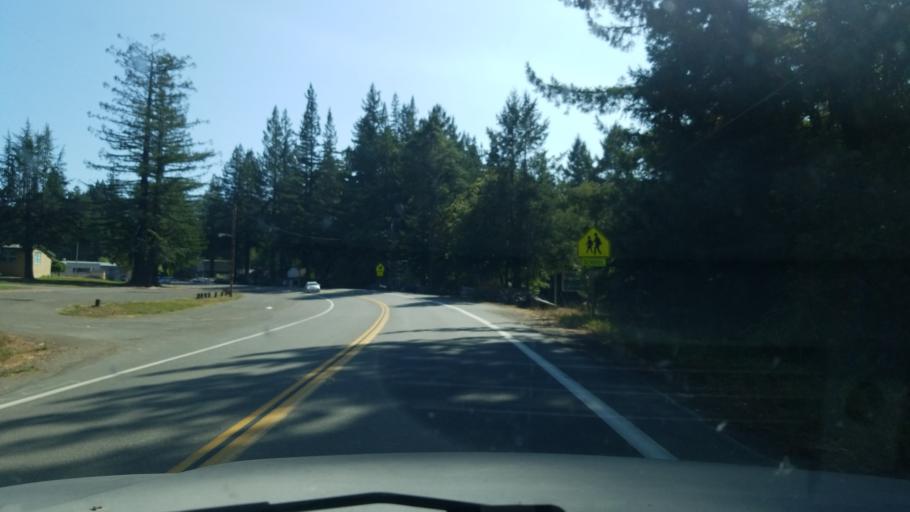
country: US
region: California
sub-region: Humboldt County
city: Redway
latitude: 40.2380
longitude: -123.8239
